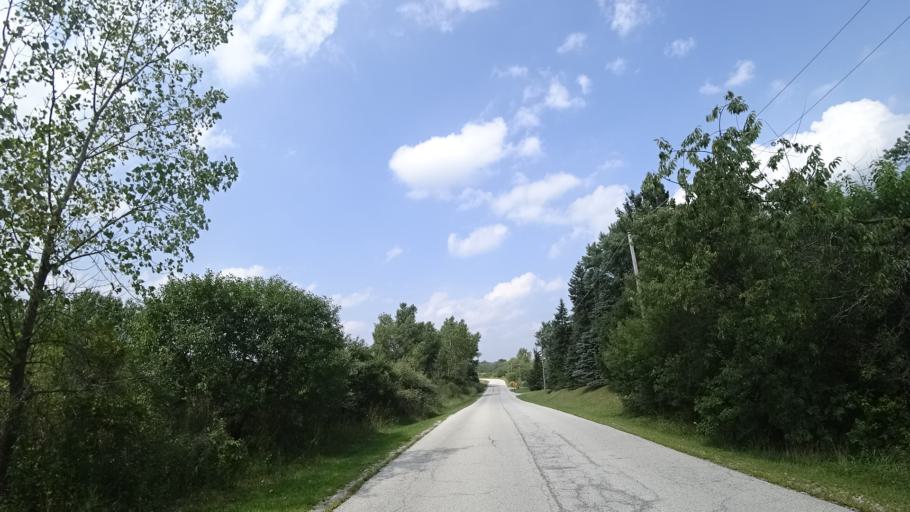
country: US
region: Illinois
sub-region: Cook County
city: Orland Park
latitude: 41.6425
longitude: -87.8879
